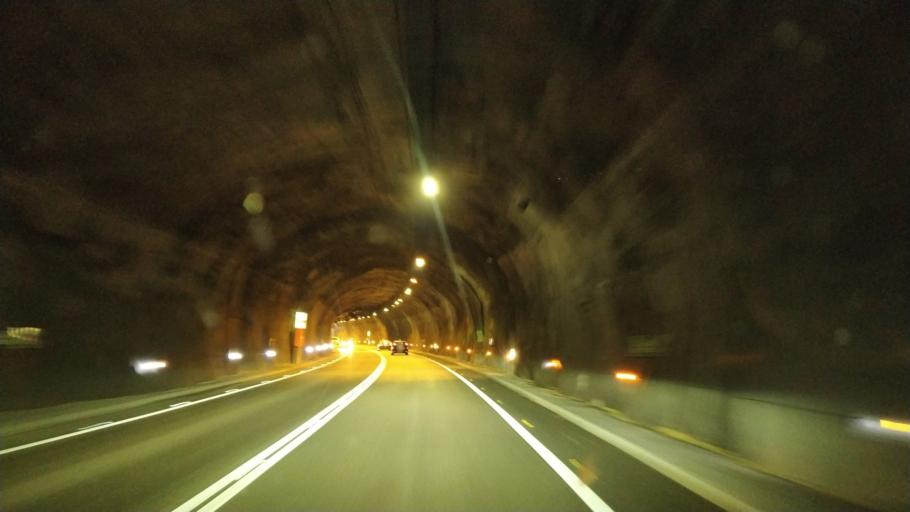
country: ES
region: Catalonia
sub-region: Provincia de Lleida
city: Coll de Nargo
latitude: 42.2543
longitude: 1.3506
